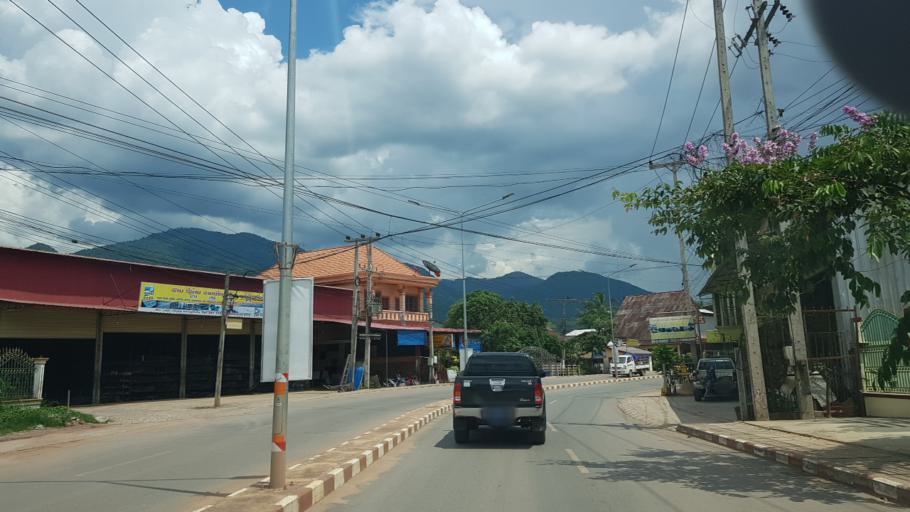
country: LA
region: Oudomxai
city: Muang Xay
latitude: 20.6788
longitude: 101.9868
